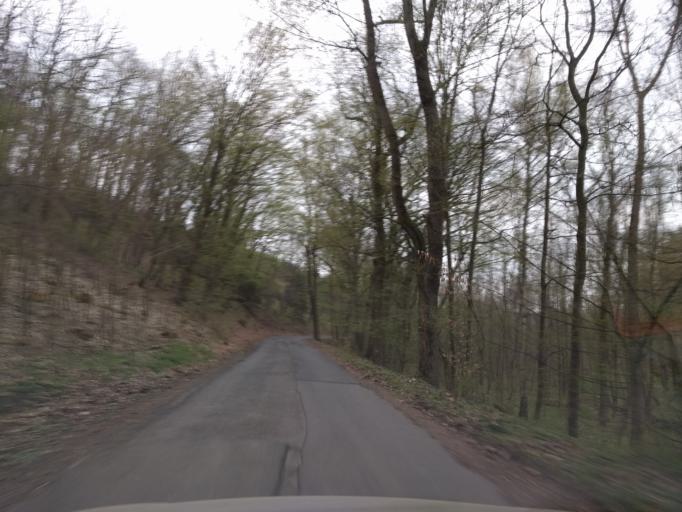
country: CZ
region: Central Bohemia
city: Kostelec nad Cernymi Lesy
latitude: 50.0180
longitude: 14.8187
